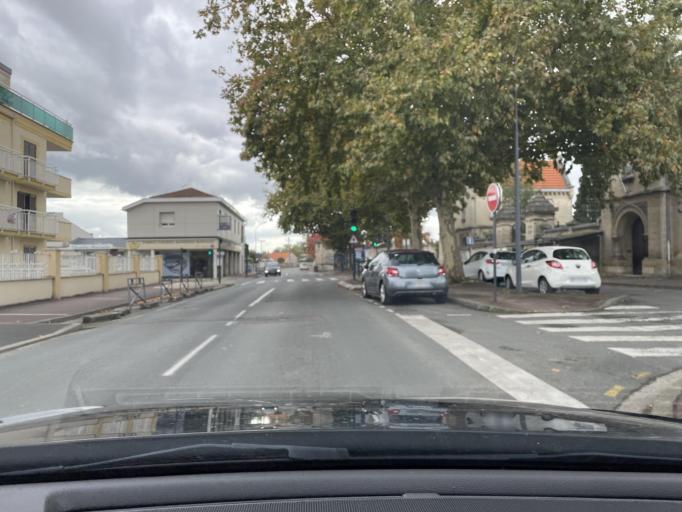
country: FR
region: Aquitaine
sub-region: Departement de la Gironde
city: Le Bouscat
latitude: 44.8762
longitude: -0.5908
